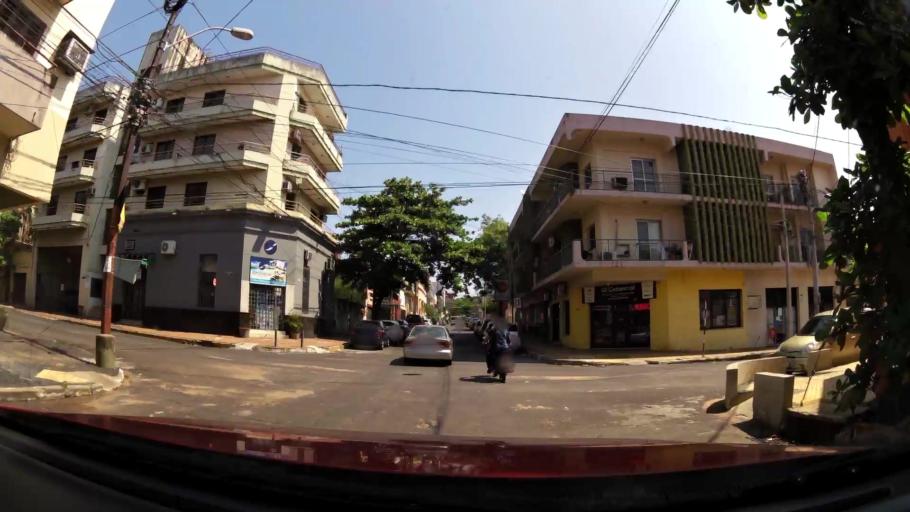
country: PY
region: Asuncion
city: Asuncion
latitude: -25.2853
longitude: -57.6408
